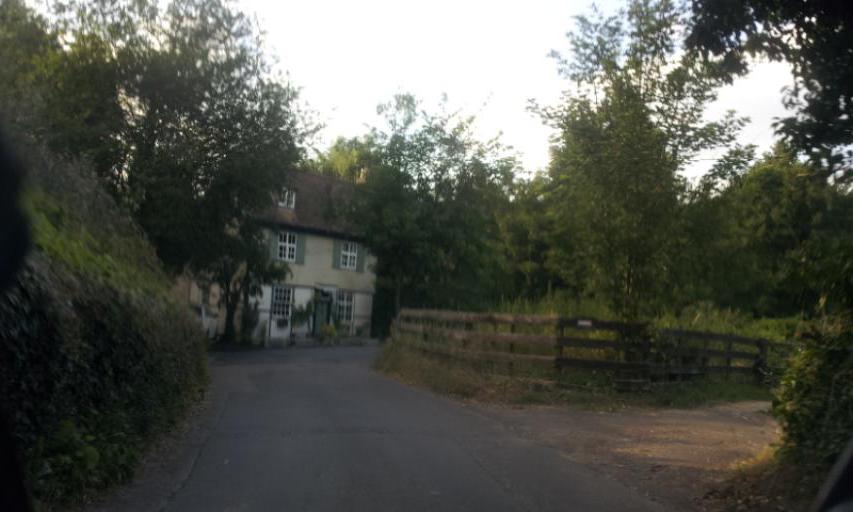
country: GB
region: England
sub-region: Kent
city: Boxley
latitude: 51.2958
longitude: 0.5160
